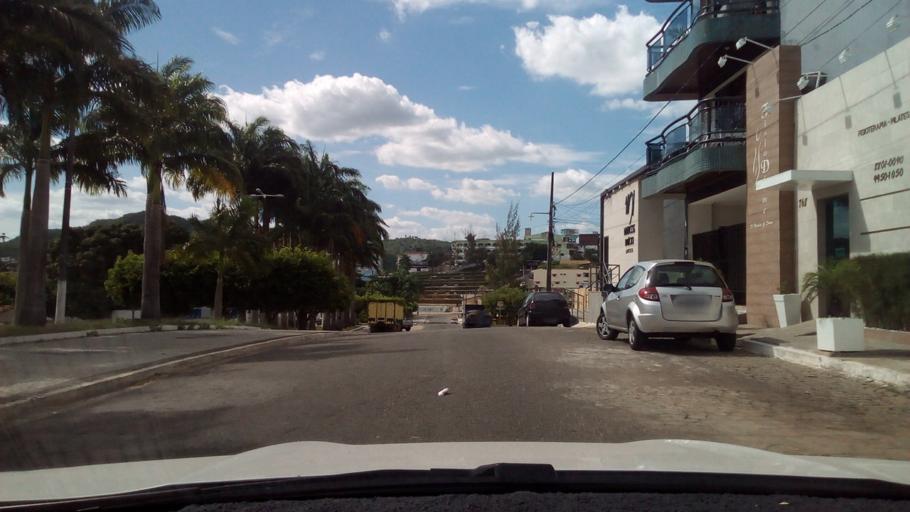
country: BR
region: Paraiba
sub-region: Guarabira
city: Guarabira
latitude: -6.8495
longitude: -35.4941
